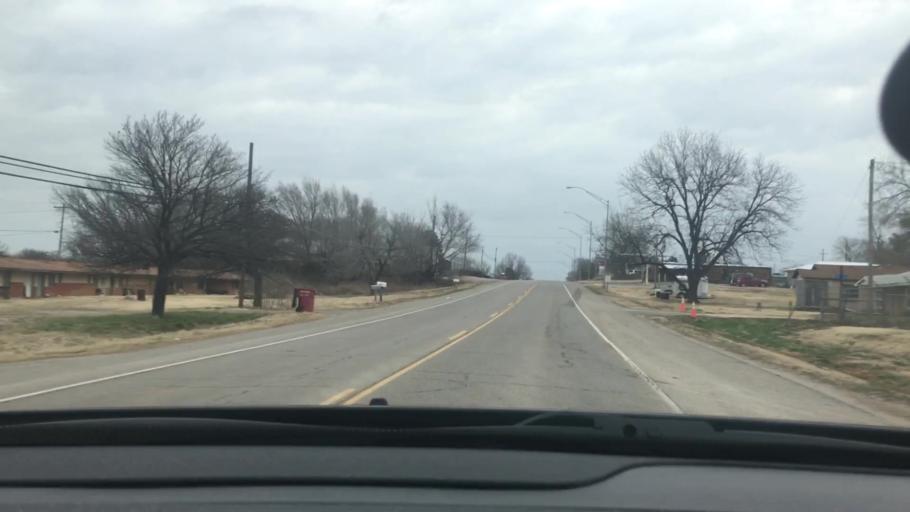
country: US
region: Oklahoma
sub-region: Garvin County
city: Maysville
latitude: 34.8188
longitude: -97.4238
